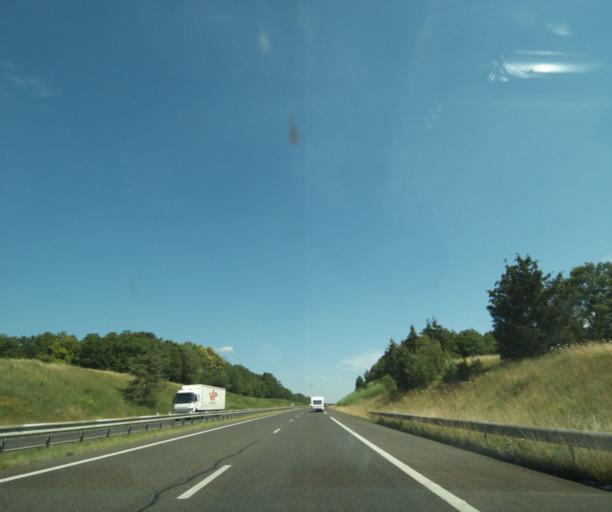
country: FR
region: Lorraine
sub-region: Departement de Meurthe-et-Moselle
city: Dommartin-les-Toul
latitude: 48.6360
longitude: 5.8813
